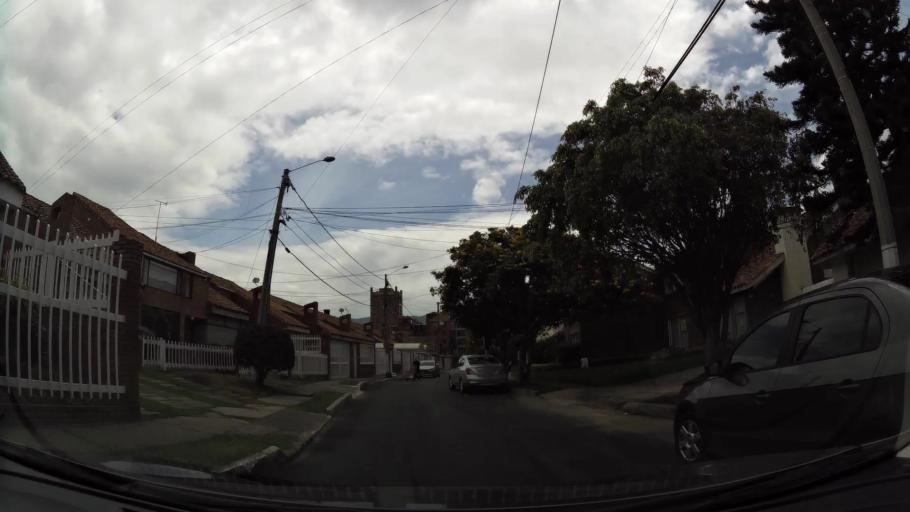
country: CO
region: Bogota D.C.
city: Barrio San Luis
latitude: 4.6984
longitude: -74.0591
